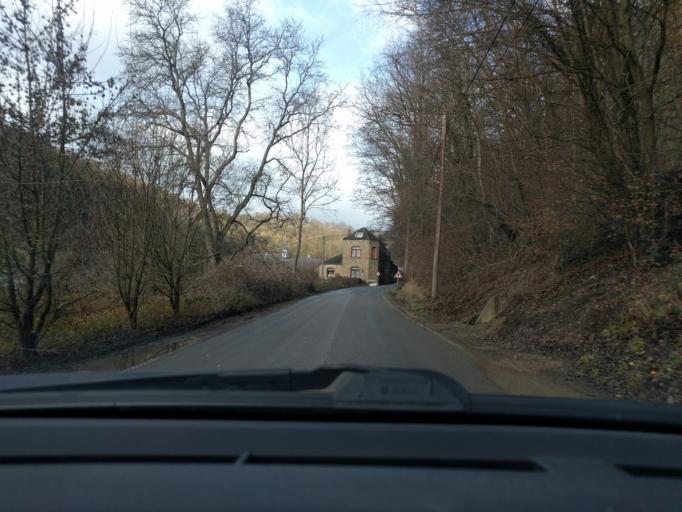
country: BE
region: Wallonia
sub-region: Province de Namur
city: Noville-les-Bois
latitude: 50.4870
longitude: 4.9595
